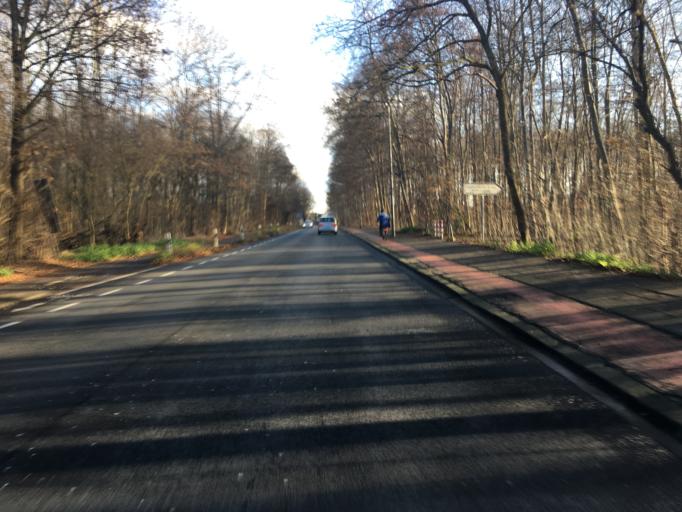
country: DE
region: North Rhine-Westphalia
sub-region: Regierungsbezirk Koln
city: Poll
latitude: 50.8846
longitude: 7.0059
